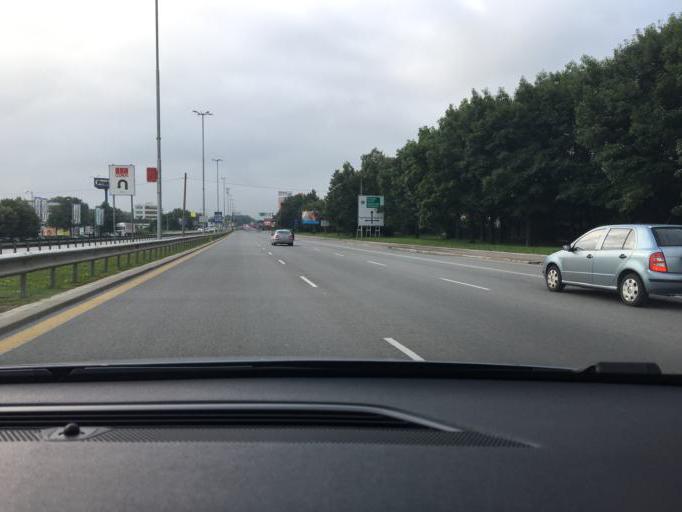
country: BG
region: Sofia-Capital
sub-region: Stolichna Obshtina
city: Sofia
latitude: 42.6407
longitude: 23.4074
